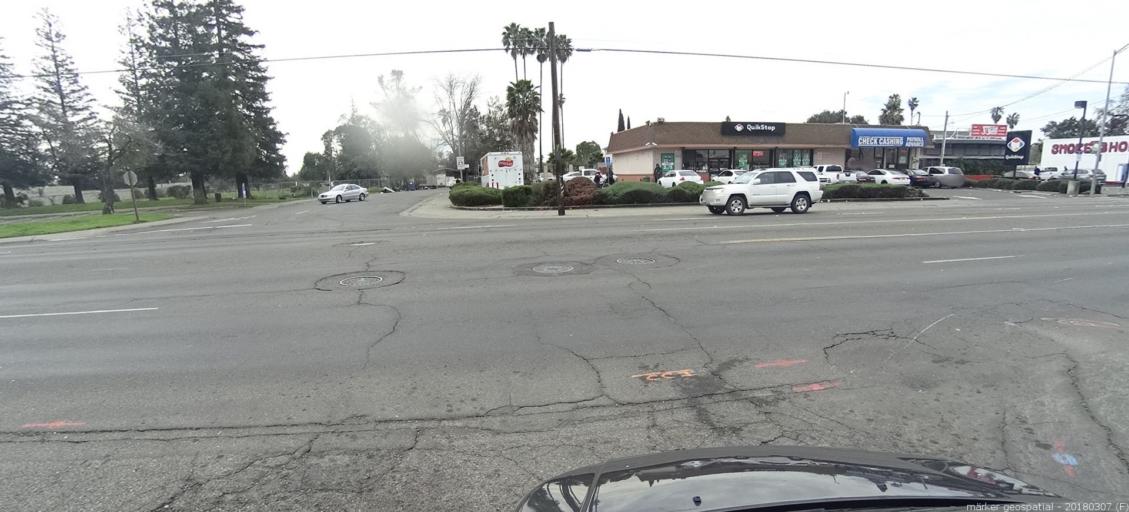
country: US
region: California
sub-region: Sacramento County
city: Parkway
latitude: 38.5250
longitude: -121.4616
